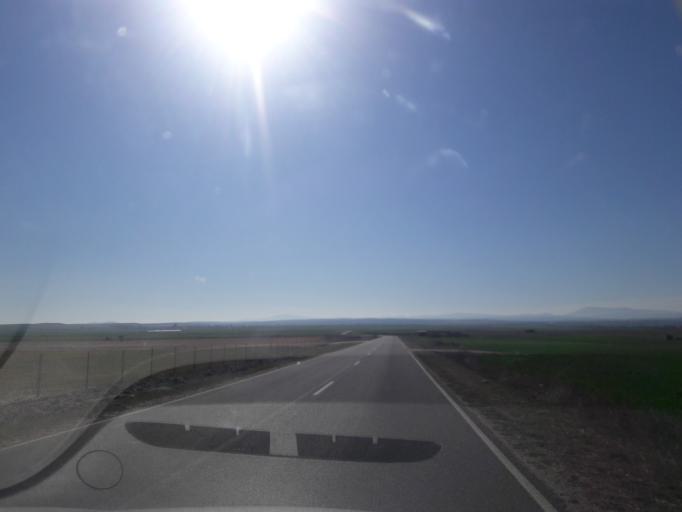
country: ES
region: Castille and Leon
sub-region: Provincia de Salamanca
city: Santiago de la Puebla
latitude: 40.8171
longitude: -5.2610
